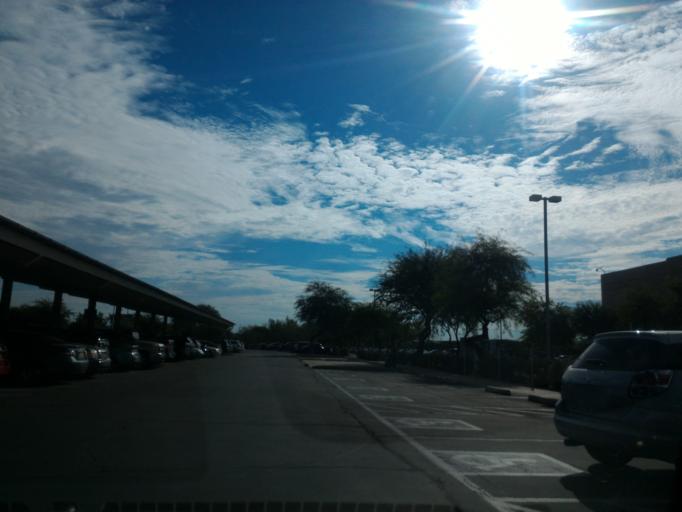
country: US
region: Arizona
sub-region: Maricopa County
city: Sun Lakes
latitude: 33.2424
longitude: -111.8810
